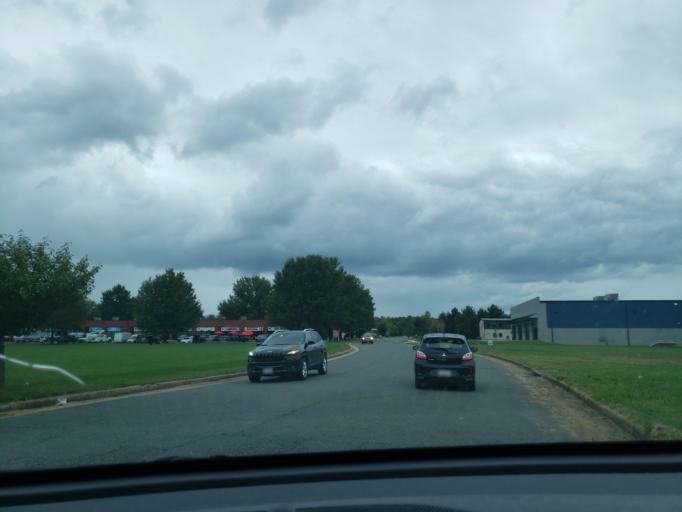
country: US
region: Virginia
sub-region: City of Fredericksburg
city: Fredericksburg
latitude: 38.2622
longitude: -77.4365
